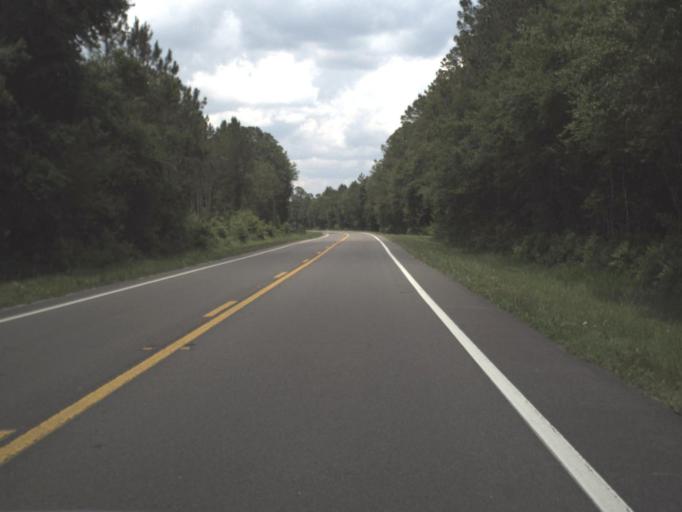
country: US
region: Florida
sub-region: Columbia County
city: Five Points
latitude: 30.2742
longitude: -82.6324
